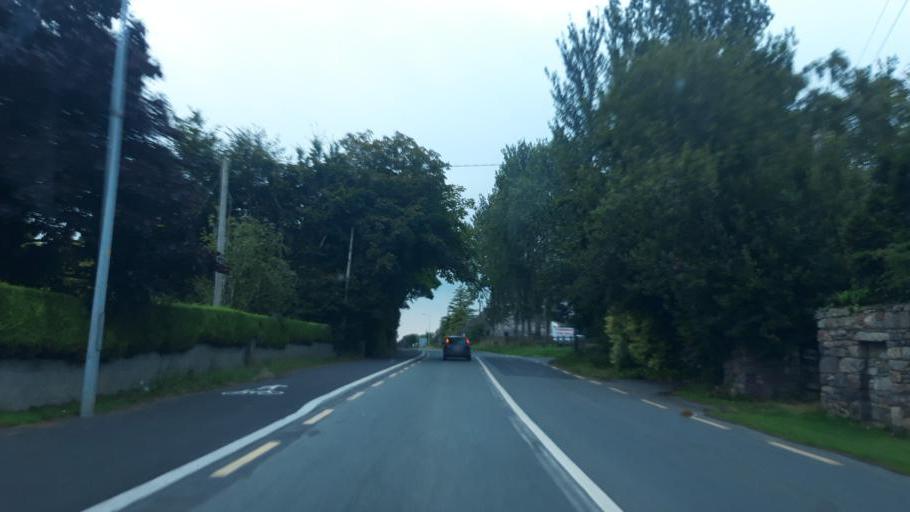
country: IE
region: Leinster
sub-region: Kilkenny
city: Thomastown
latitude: 52.5349
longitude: -7.1386
